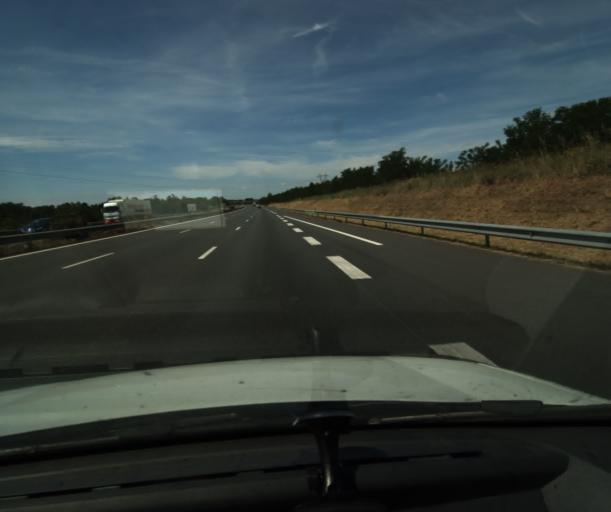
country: FR
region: Midi-Pyrenees
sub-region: Departement du Tarn-et-Garonne
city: Campsas
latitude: 43.8921
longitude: 1.3174
